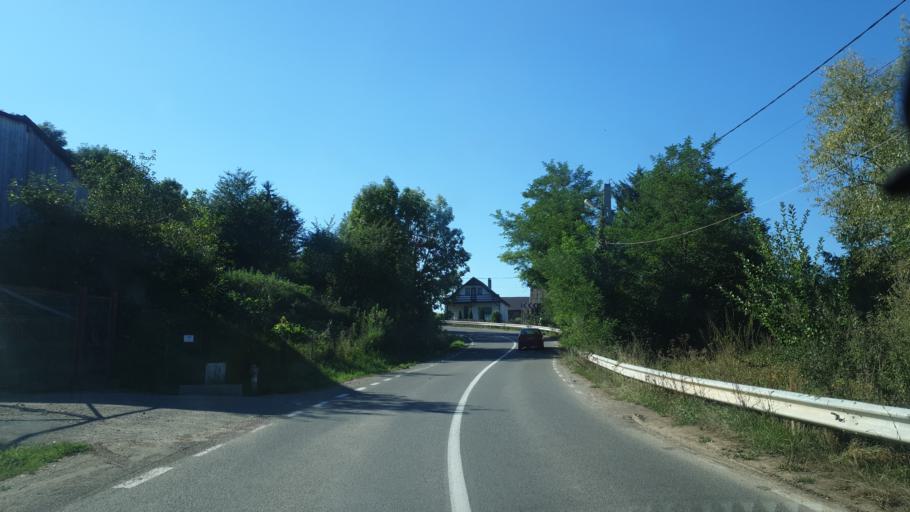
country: RO
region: Covasna
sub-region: Comuna Ilieni
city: Ilieni
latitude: 45.7858
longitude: 25.7588
